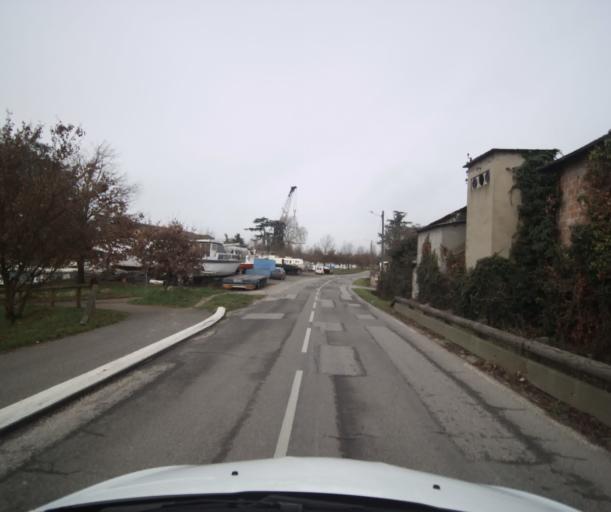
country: FR
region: Midi-Pyrenees
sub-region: Departement du Tarn-et-Garonne
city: Castelsarrasin
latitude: 44.0384
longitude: 1.1154
